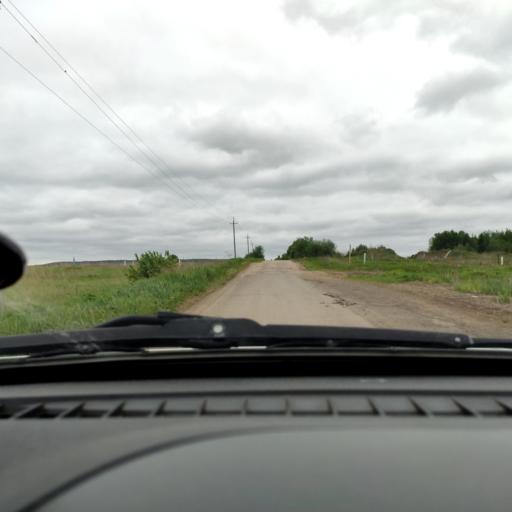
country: RU
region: Perm
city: Gamovo
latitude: 57.8591
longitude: 56.0846
